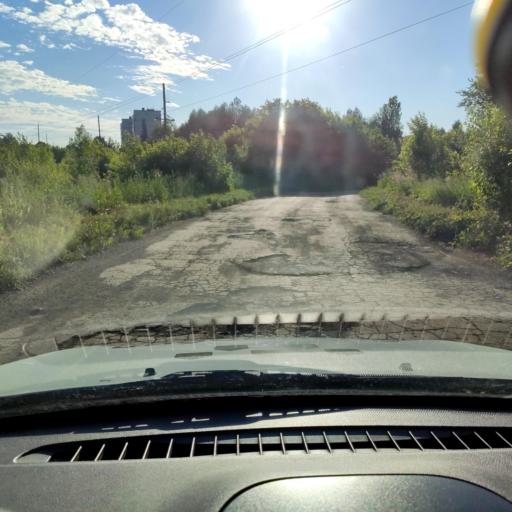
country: RU
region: Samara
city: Zhigulevsk
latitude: 53.3989
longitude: 49.5467
